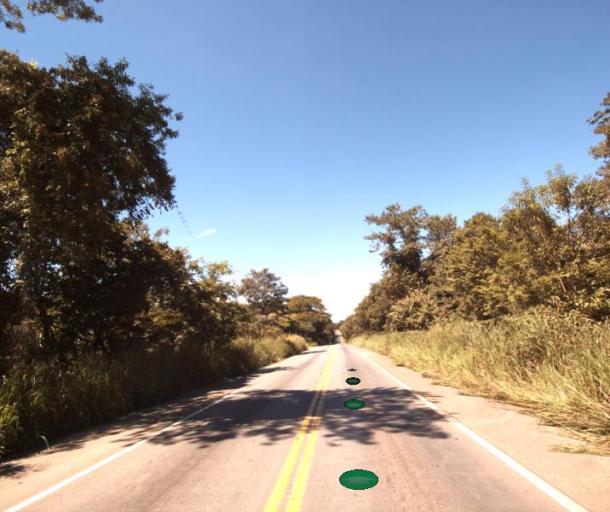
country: BR
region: Goias
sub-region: Jaragua
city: Jaragua
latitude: -15.6012
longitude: -49.4059
